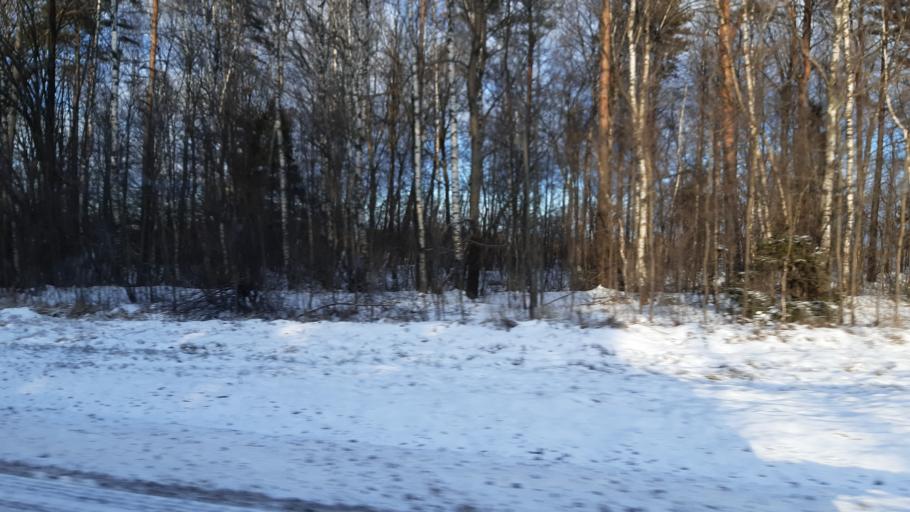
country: RU
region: Moskovskaya
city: Svatkovo
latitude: 56.3082
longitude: 38.3258
